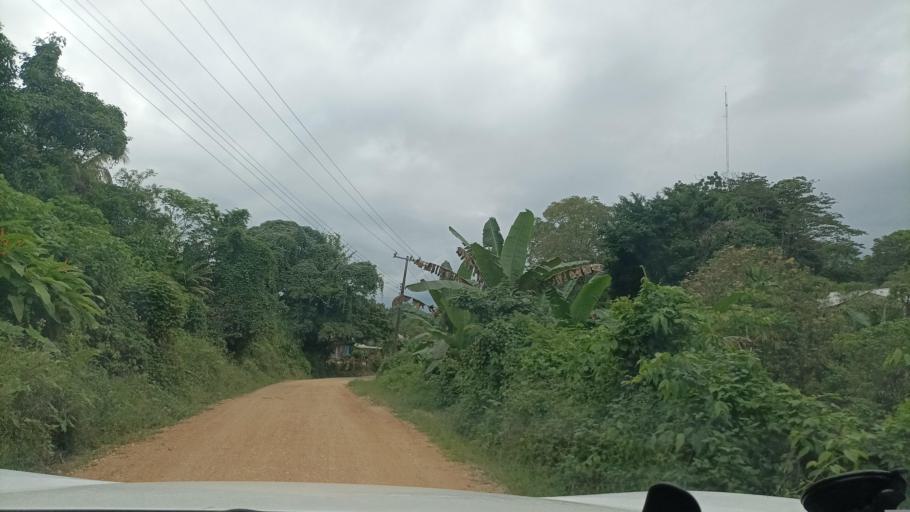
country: MX
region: Veracruz
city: Hidalgotitlan
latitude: 17.6369
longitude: -94.5122
